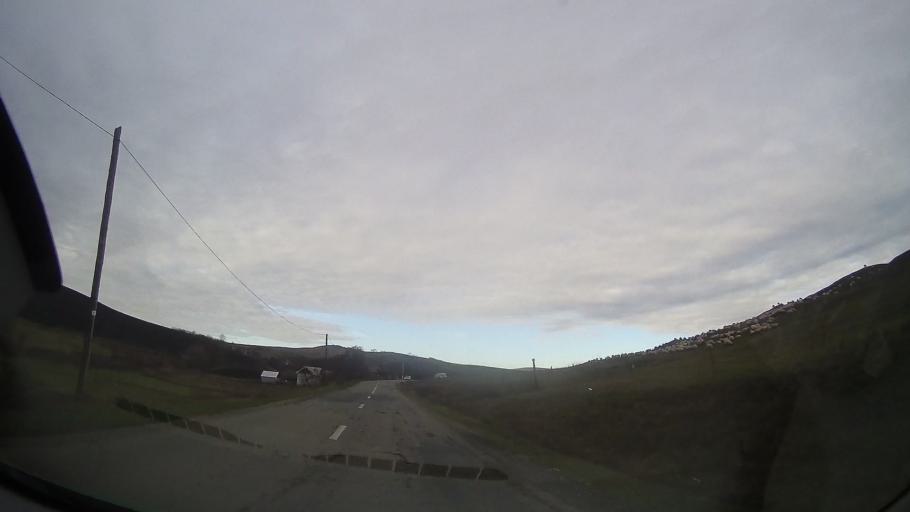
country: RO
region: Cluj
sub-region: Comuna Camarasu
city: Camarasu
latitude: 46.8133
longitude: 24.1422
